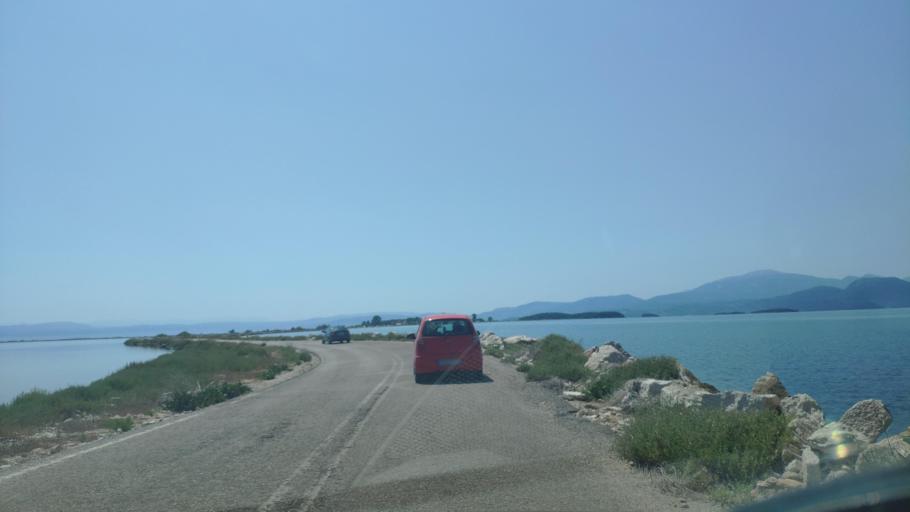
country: GR
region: Epirus
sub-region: Nomos Artas
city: Aneza
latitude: 39.0294
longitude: 20.9005
